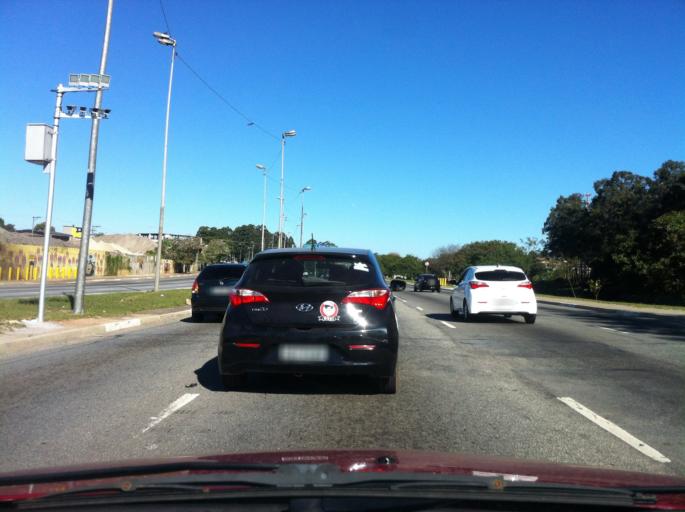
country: BR
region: Sao Paulo
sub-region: Guarulhos
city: Guarulhos
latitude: -23.5026
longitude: -46.4586
